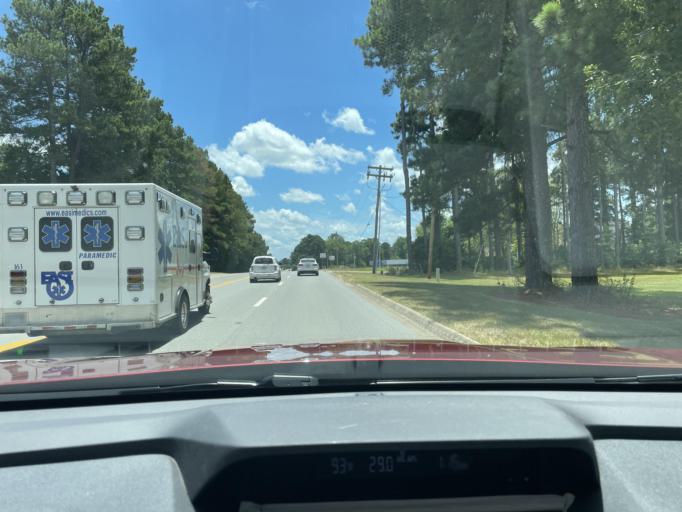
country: US
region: Arkansas
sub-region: Drew County
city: Monticello
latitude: 33.6537
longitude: -91.8026
